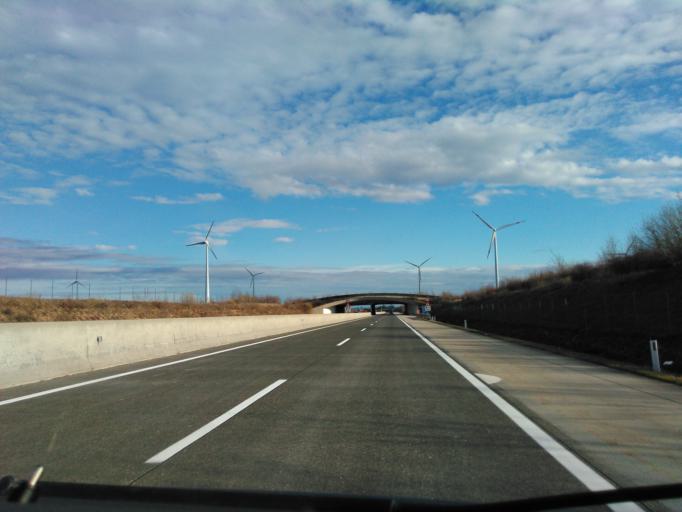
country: AT
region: Burgenland
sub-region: Politischer Bezirk Neusiedl am See
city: Potzneusiedl
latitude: 48.0361
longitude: 16.9121
